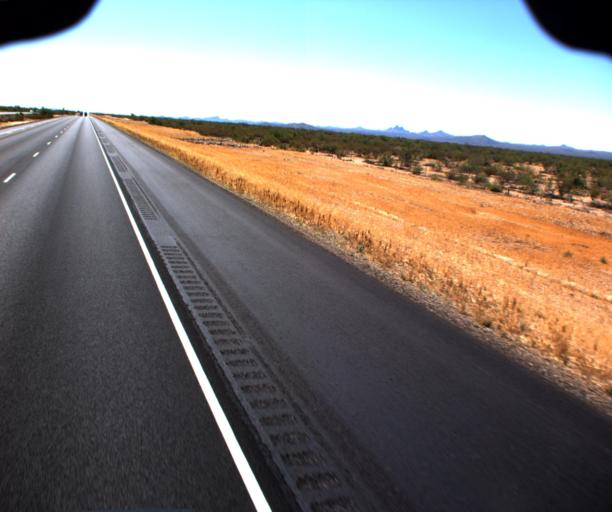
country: US
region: Arizona
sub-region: Yavapai County
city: Congress
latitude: 34.0836
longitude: -112.8939
